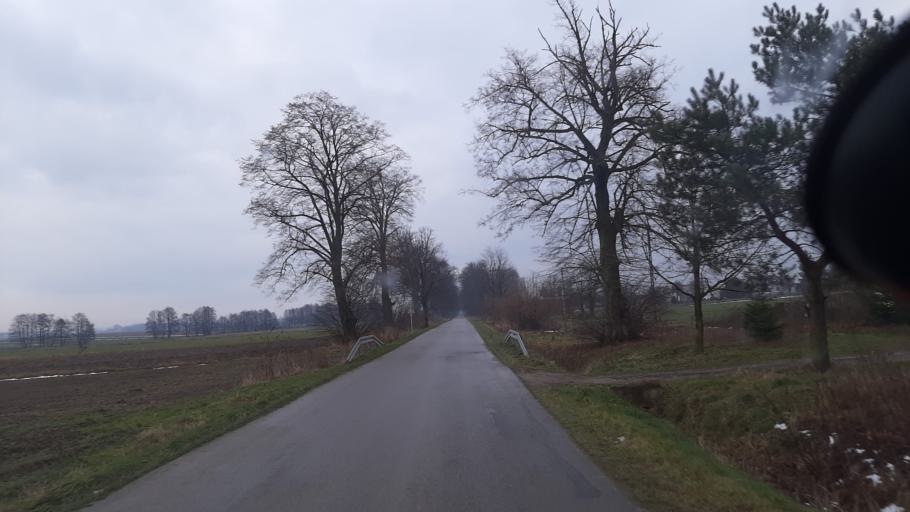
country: PL
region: Lublin Voivodeship
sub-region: Powiat lubelski
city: Jastkow
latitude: 51.3483
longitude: 22.5177
